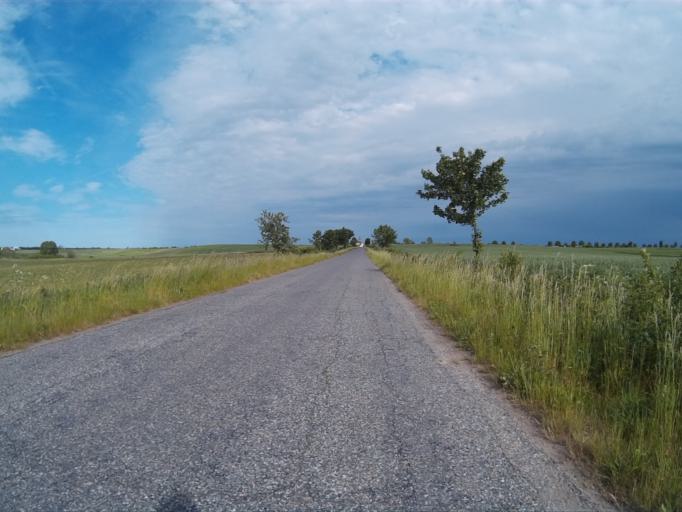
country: PL
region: Kujawsko-Pomorskie
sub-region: Powiat tucholski
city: Lubiewo
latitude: 53.4680
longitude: 18.0046
